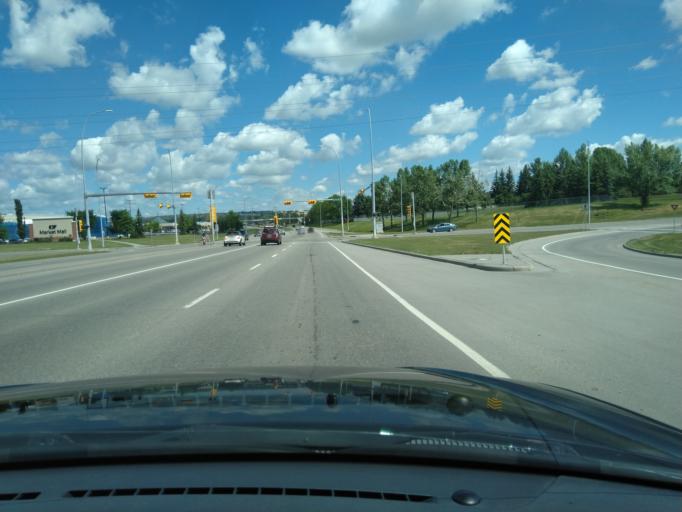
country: CA
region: Alberta
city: Calgary
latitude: 51.0808
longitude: -114.1521
